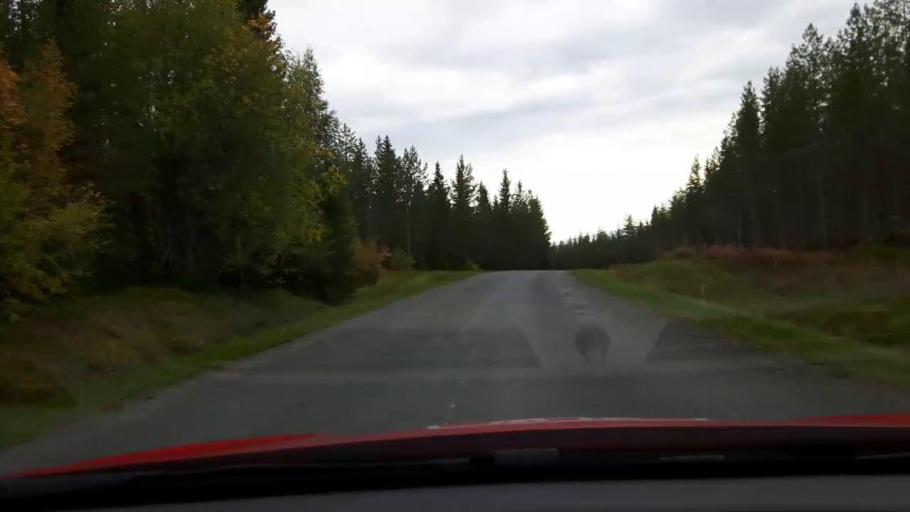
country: SE
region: Jaemtland
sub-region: Krokoms Kommun
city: Krokom
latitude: 63.2146
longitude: 14.1189
